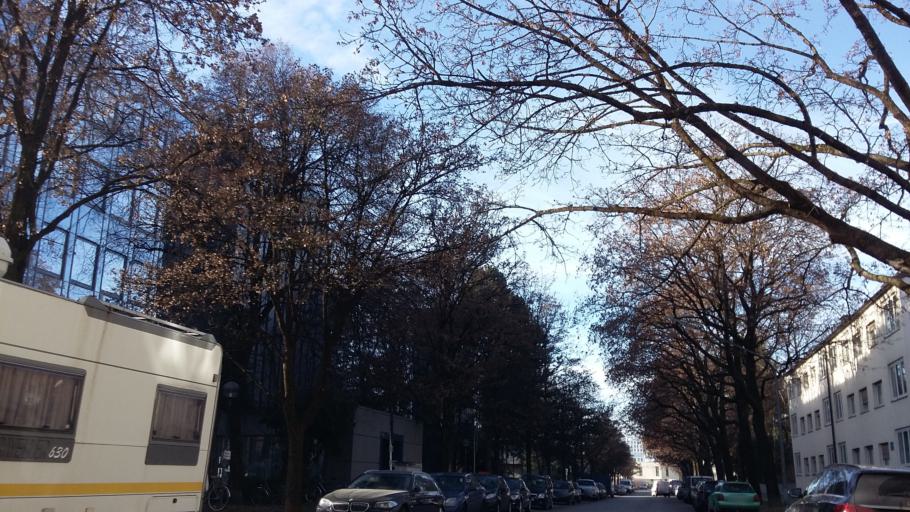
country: DE
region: Bavaria
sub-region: Upper Bavaria
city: Munich
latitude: 48.1458
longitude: 11.5301
